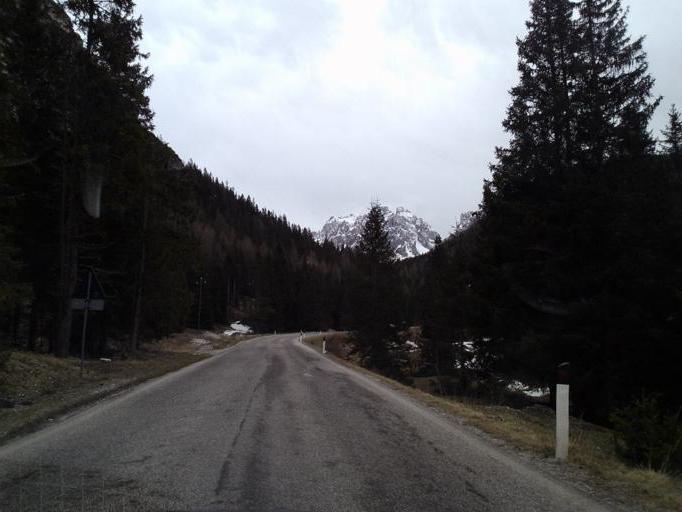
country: IT
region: Veneto
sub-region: Provincia di Belluno
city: Cortina d'Ampezzo
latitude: 46.6051
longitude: 12.2380
